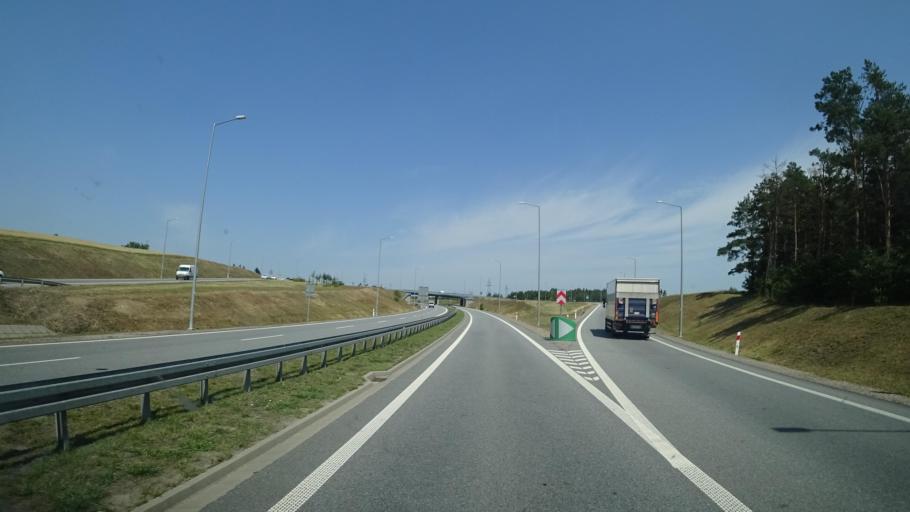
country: PL
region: Pomeranian Voivodeship
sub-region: Powiat koscierski
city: Koscierzyna
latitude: 54.1211
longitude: 18.0182
